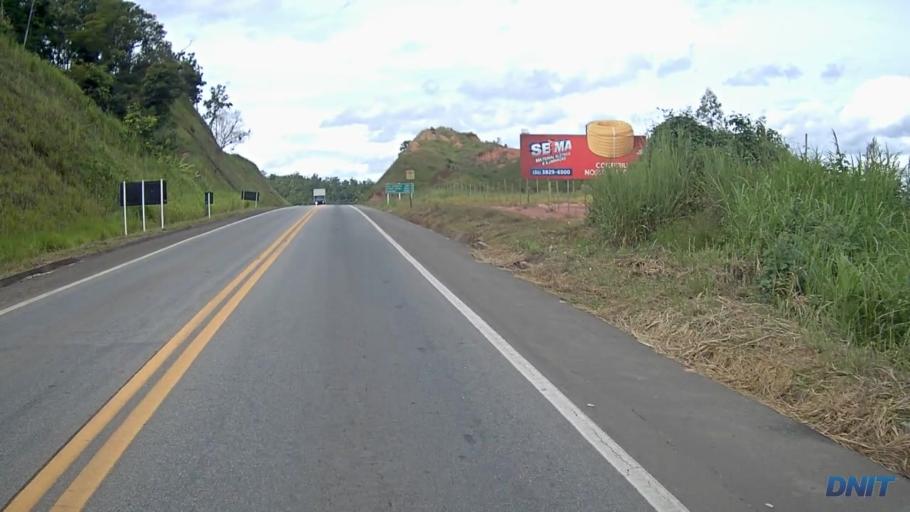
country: BR
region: Minas Gerais
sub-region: Ipatinga
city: Ipatinga
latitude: -19.4517
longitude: -42.5188
